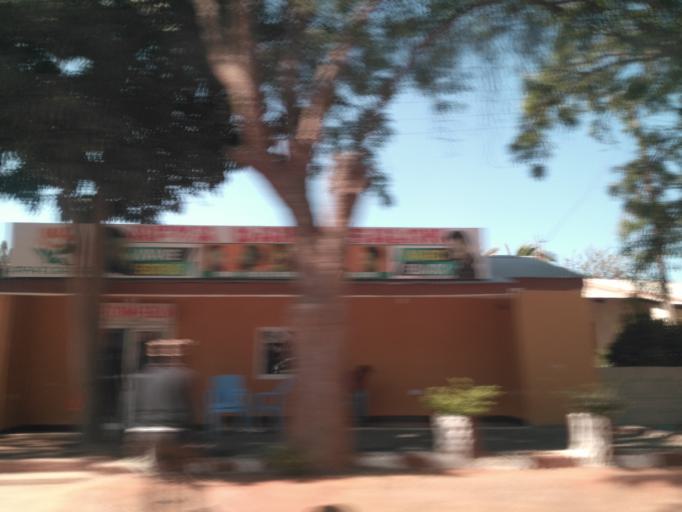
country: TZ
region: Dodoma
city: Dodoma
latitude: -6.1661
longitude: 35.7495
